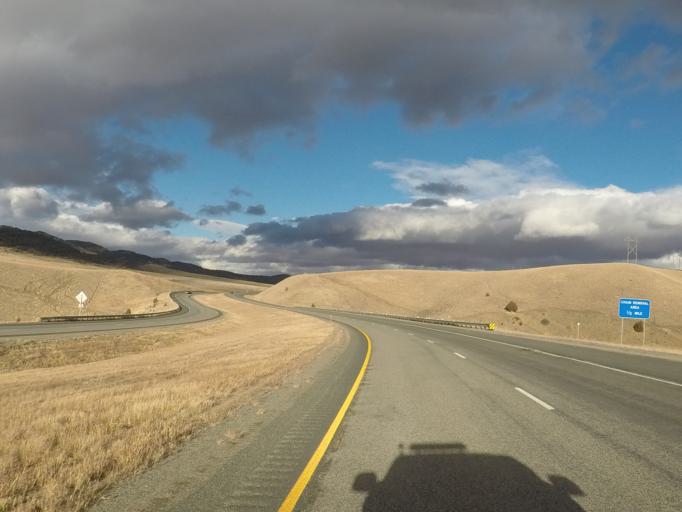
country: US
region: Montana
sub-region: Jefferson County
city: Whitehall
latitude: 45.8802
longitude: -111.8730
